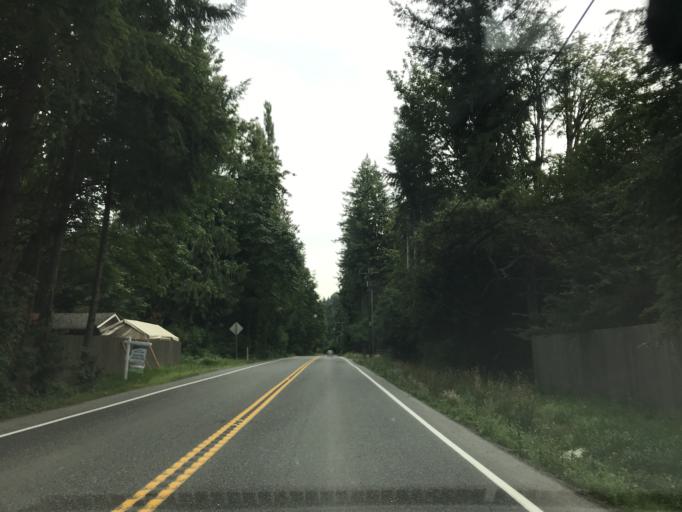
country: US
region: Washington
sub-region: King County
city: Fall City
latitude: 47.5590
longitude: -121.8954
